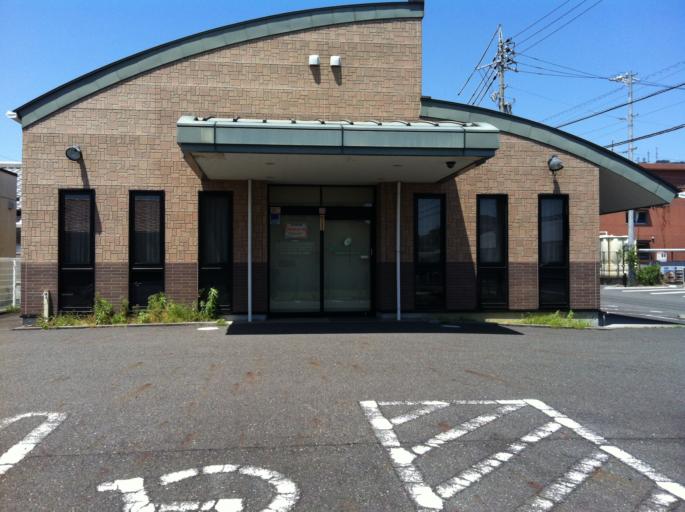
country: JP
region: Shizuoka
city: Shizuoka-shi
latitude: 35.0324
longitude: 138.4534
